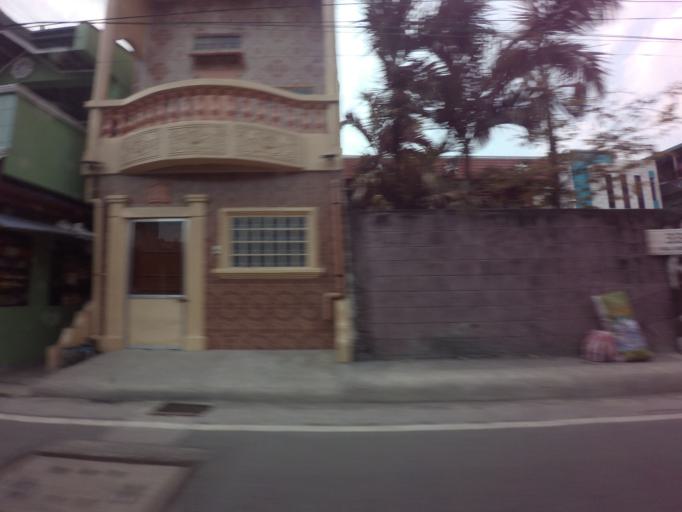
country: PH
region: Calabarzon
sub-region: Province of Rizal
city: Taguig
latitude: 14.4743
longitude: 121.0593
